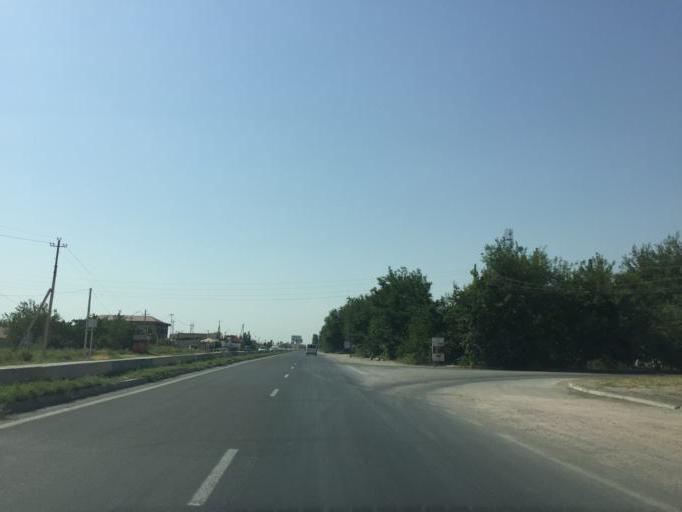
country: AM
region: Ararat
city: Artashat
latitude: 39.9508
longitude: 44.5423
